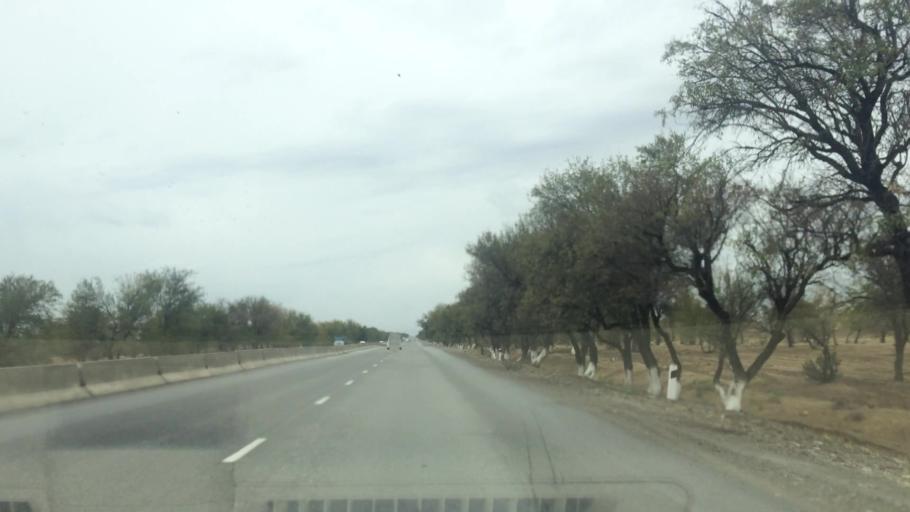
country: UZ
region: Samarqand
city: Bulung'ur
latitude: 39.8296
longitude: 67.4101
